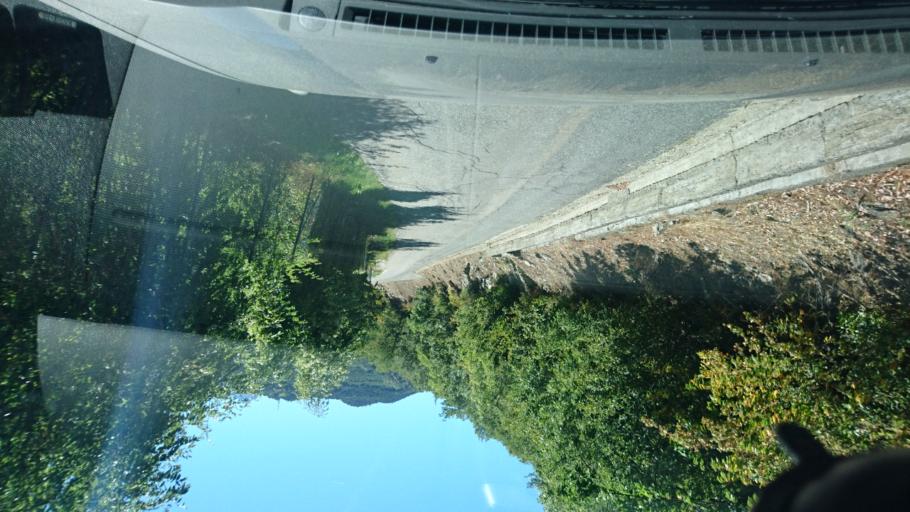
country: IT
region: Aosta Valley
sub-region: Valle d'Aosta
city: Avise
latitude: 45.7112
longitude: 7.1344
